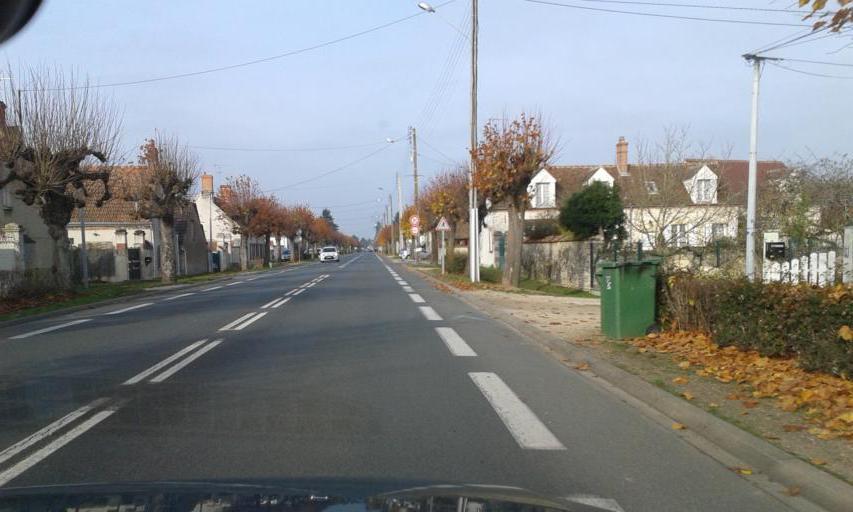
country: FR
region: Centre
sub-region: Departement du Loiret
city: Olivet
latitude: 47.8505
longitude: 1.9082
